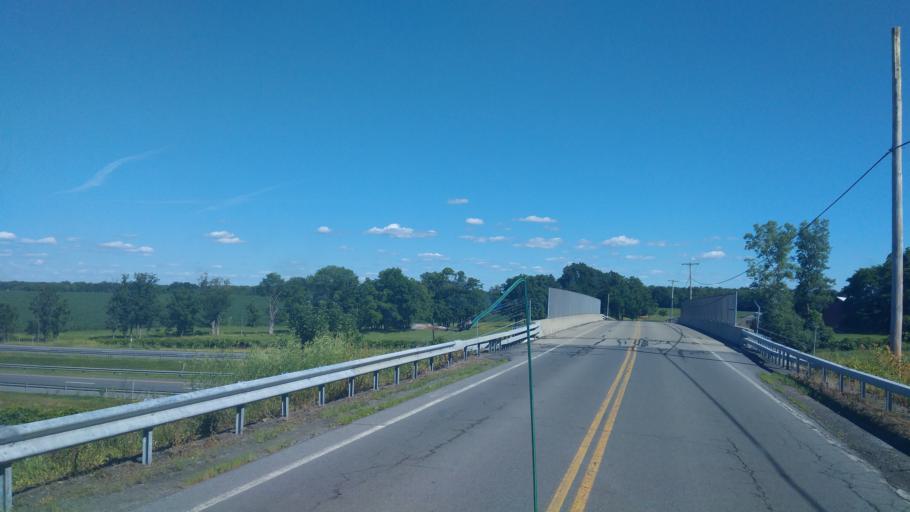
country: US
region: New York
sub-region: Seneca County
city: Seneca Falls
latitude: 42.9805
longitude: -76.7987
